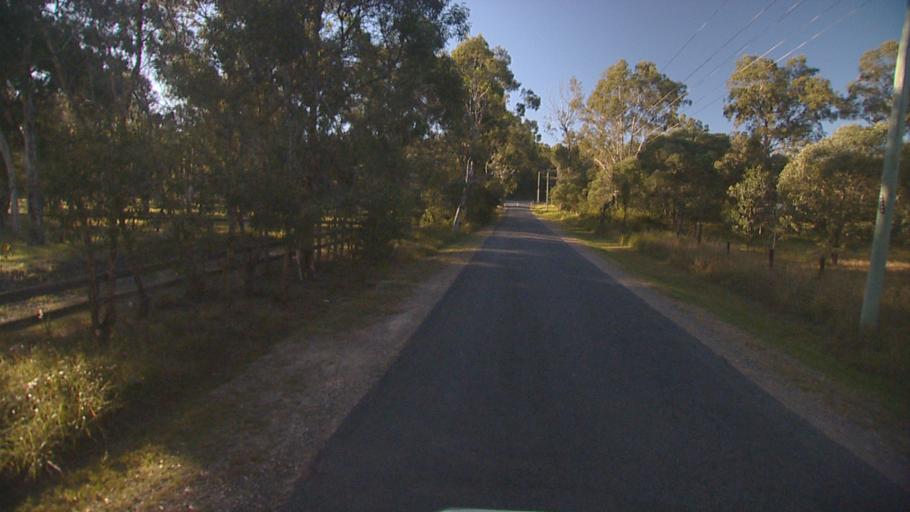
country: AU
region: Queensland
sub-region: Logan
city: Chambers Flat
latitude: -27.7706
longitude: 153.1298
